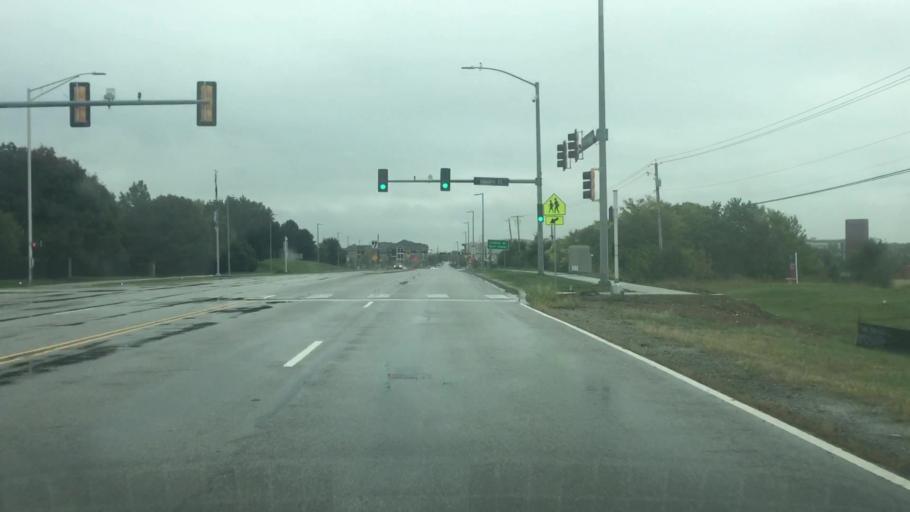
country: US
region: Kansas
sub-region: Johnson County
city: Lenexa
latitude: 38.9710
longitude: -94.7939
